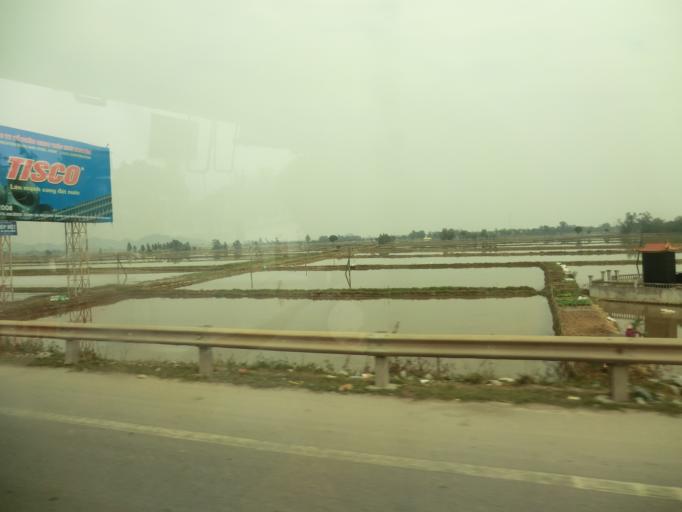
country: VN
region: Ha Nam
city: Thi Tran Thanh Luu
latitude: 20.3986
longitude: 105.9190
